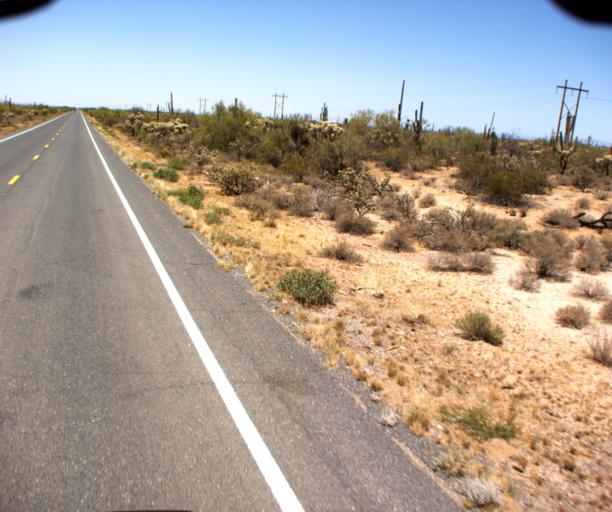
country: US
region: Arizona
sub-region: Pinal County
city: Florence
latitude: 32.8528
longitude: -111.2329
